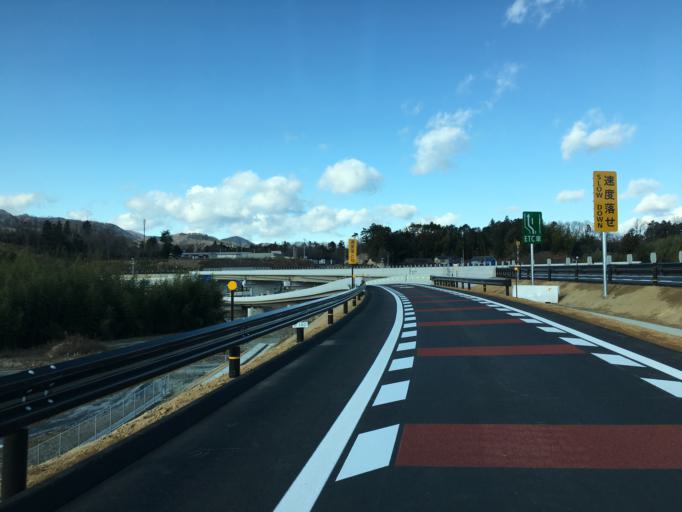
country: JP
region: Miyagi
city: Marumori
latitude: 37.7822
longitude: 140.9015
